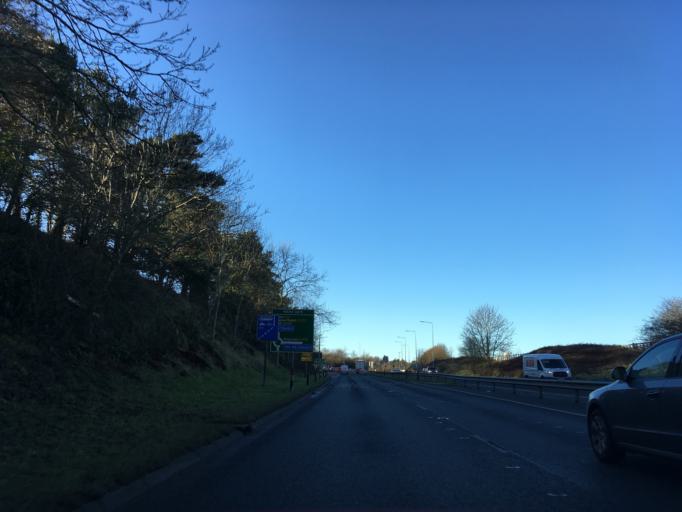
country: GB
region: England
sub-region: Bath and North East Somerset
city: Keynsham
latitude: 51.4242
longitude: -2.5124
